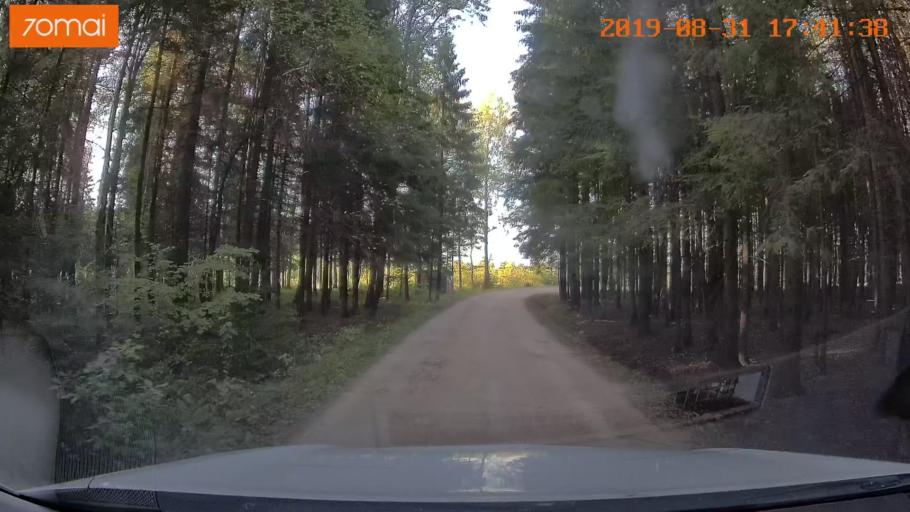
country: RU
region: Kaluga
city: Detchino
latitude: 54.8212
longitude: 36.3653
